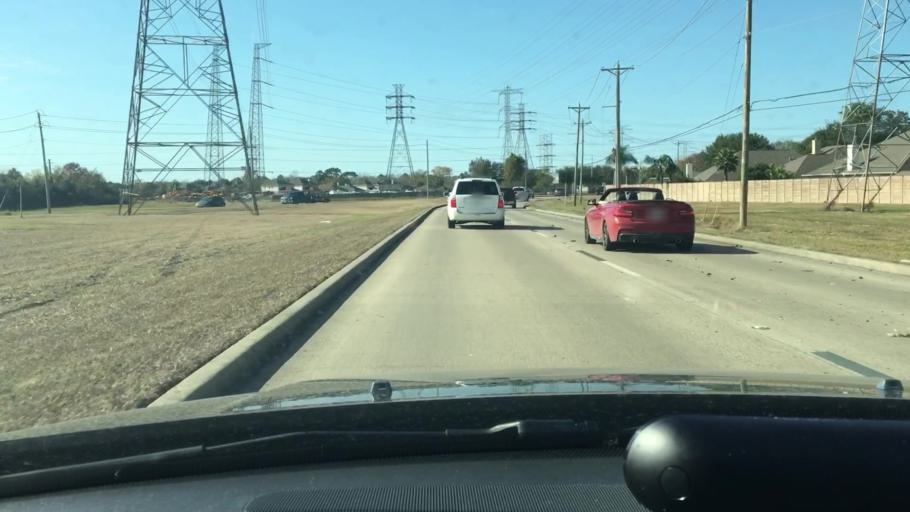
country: US
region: Texas
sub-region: Galveston County
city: League City
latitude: 29.4920
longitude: -95.0824
